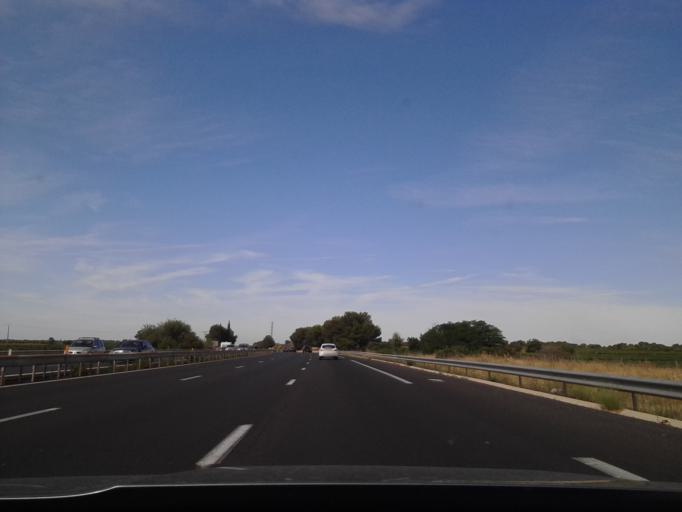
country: FR
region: Languedoc-Roussillon
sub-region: Departement de l'Herault
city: Pinet
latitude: 43.4195
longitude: 3.5287
